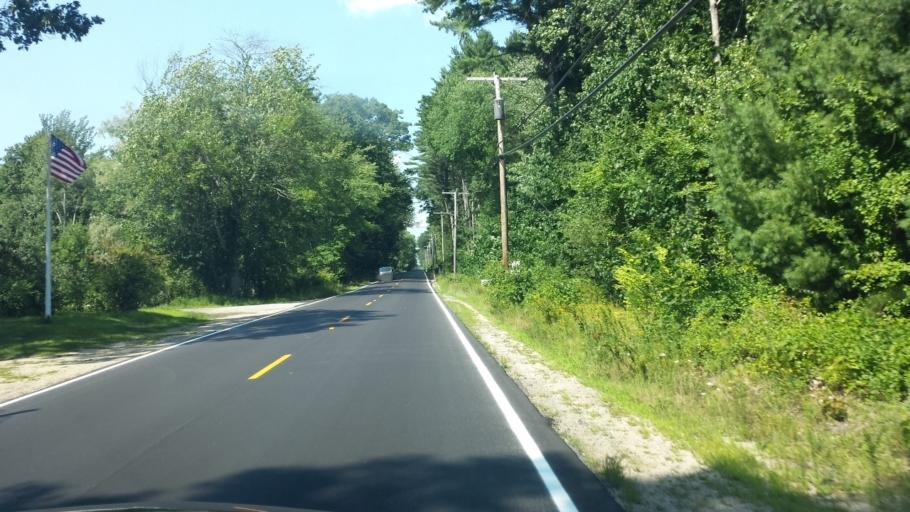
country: US
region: Maine
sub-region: York County
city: Arundel
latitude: 43.3932
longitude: -70.4830
